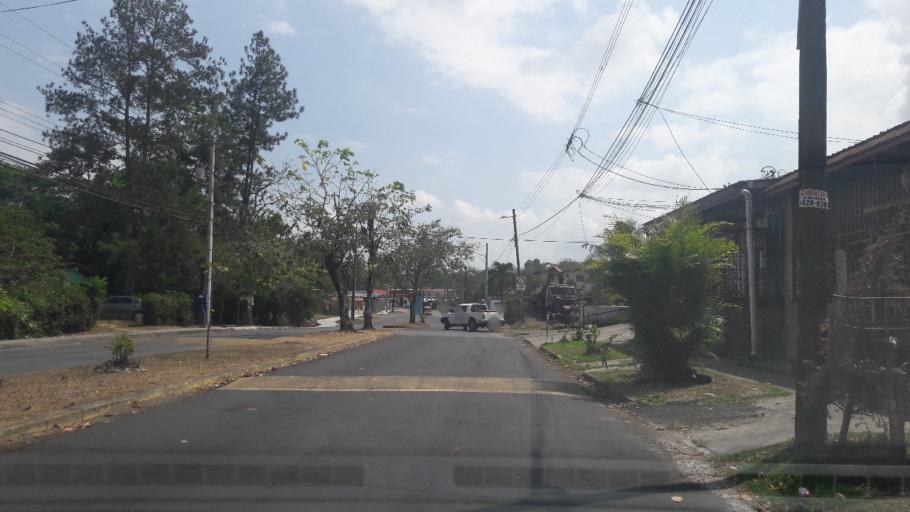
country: PA
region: Panama
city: Alcalde Diaz
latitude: 9.1300
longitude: -79.5474
